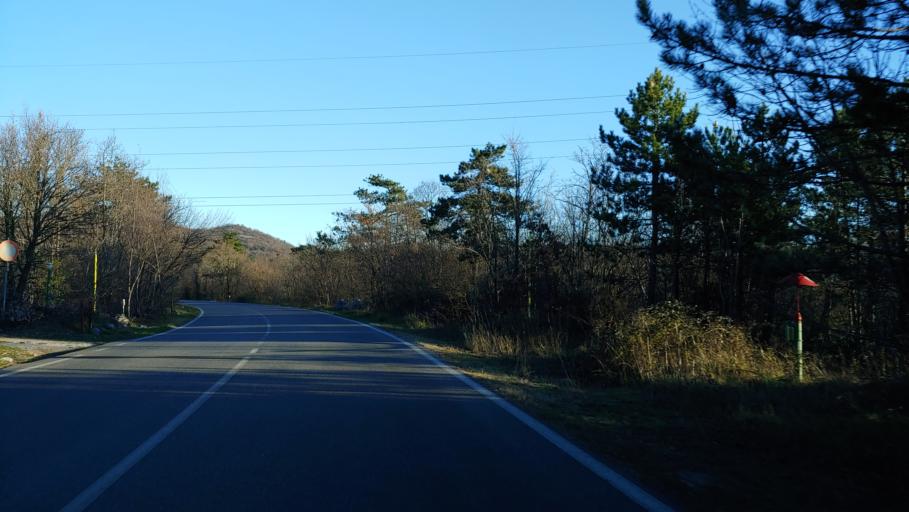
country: IT
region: Friuli Venezia Giulia
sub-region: Provincia di Trieste
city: Zolla
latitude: 45.7023
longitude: 13.8003
